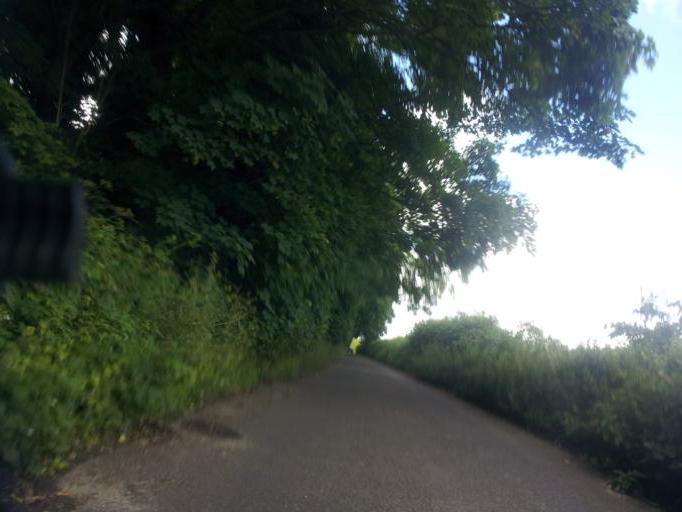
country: GB
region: England
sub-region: Kent
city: West Malling
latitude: 51.3109
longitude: 0.3828
